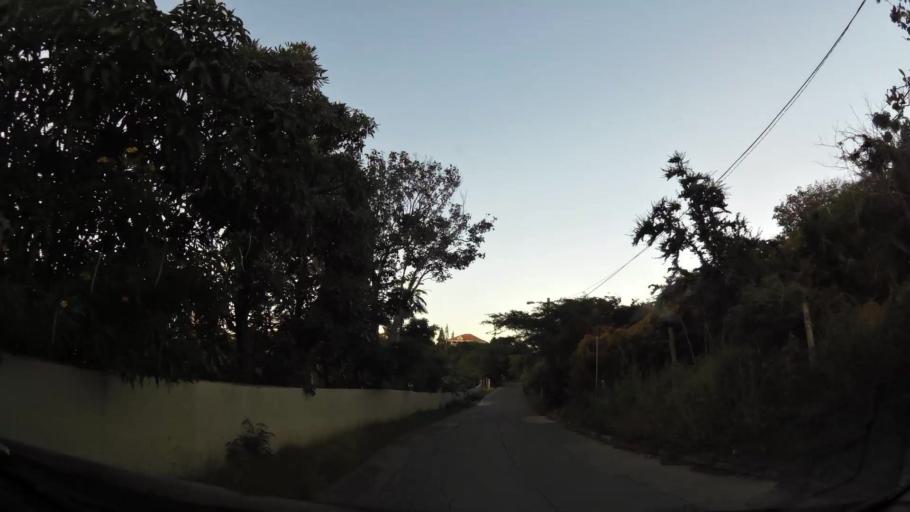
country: VG
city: Tortola
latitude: 18.4482
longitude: -64.5762
